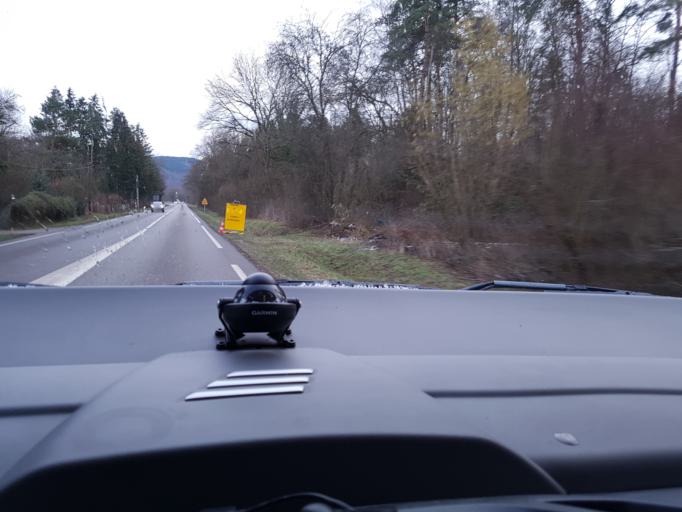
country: FR
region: Alsace
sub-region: Departement du Bas-Rhin
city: Chatenois
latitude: 48.2991
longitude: 7.3560
